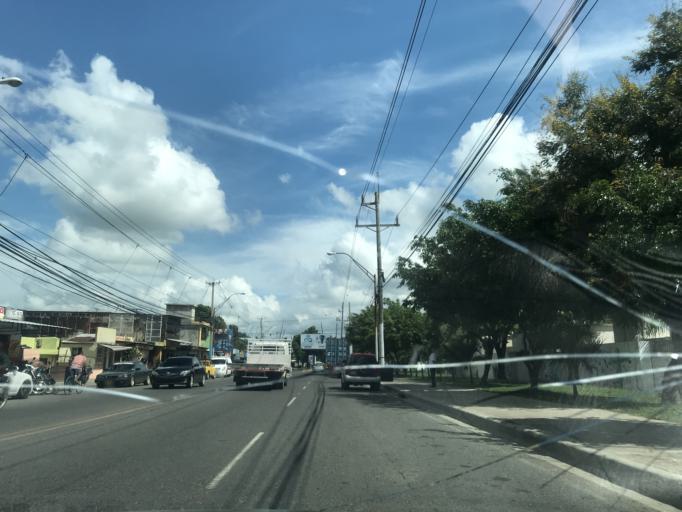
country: DO
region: Santiago
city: Palmar Arriba
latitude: 19.4912
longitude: -70.7361
